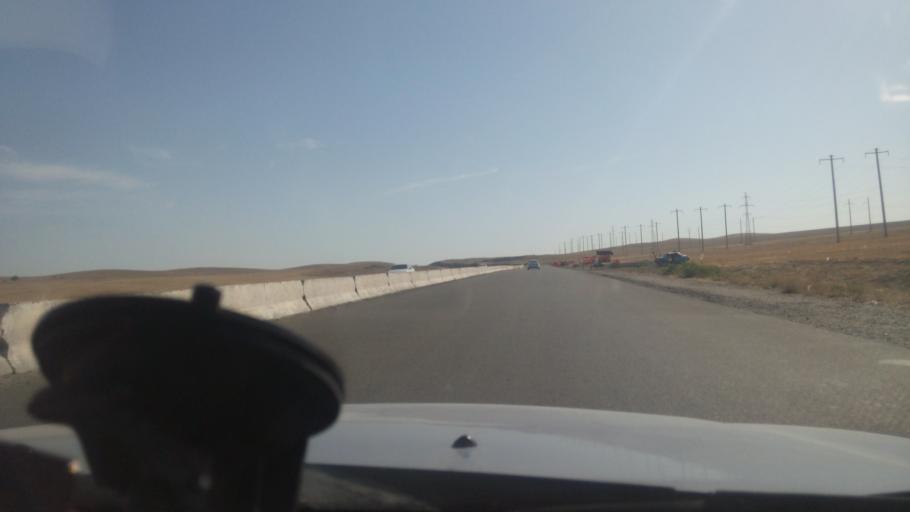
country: UZ
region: Jizzax
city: Jizzax
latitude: 40.0447
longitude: 67.6682
